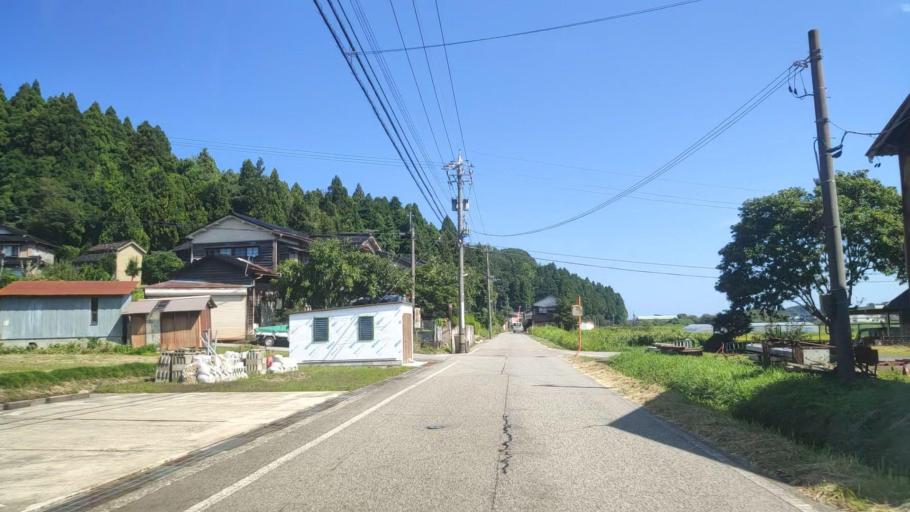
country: JP
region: Ishikawa
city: Nanao
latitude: 37.3805
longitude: 136.8811
